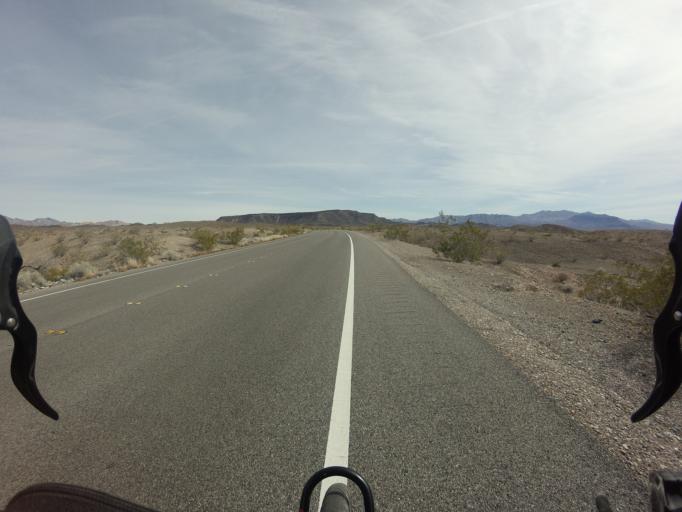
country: US
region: Nevada
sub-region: Clark County
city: Boulder City
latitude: 36.1573
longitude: -114.8057
